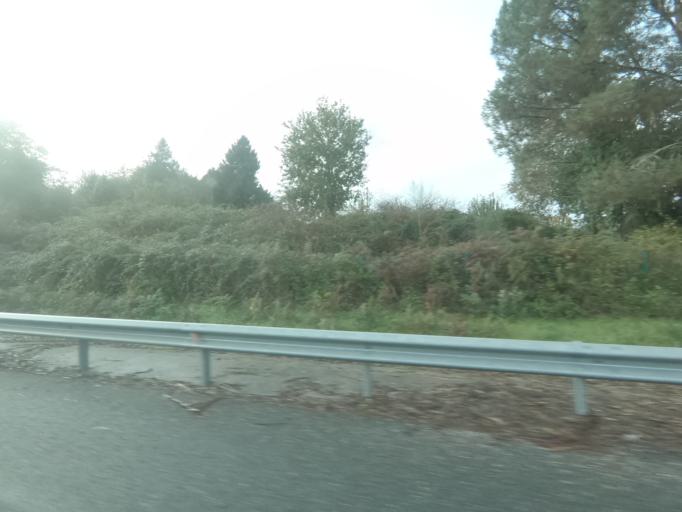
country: ES
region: Galicia
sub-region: Provincia de Pontevedra
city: Tui
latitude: 42.0679
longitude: -8.6421
